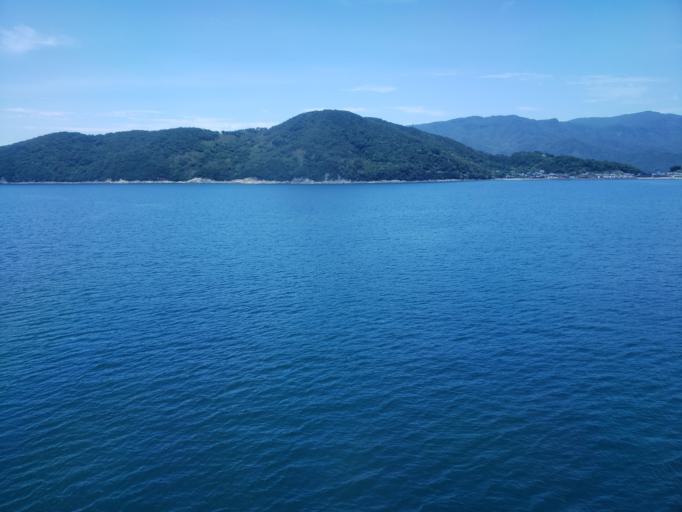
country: JP
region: Kagawa
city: Tonosho
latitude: 34.4450
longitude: 134.3076
